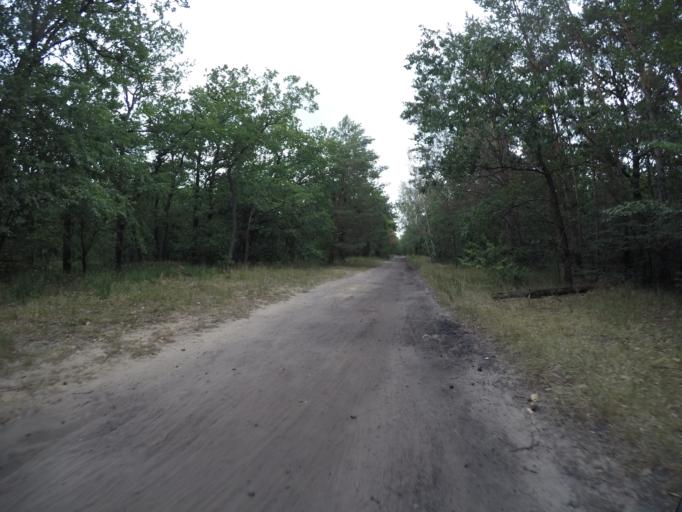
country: DE
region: Berlin
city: Johannisthal
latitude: 52.4550
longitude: 13.4950
